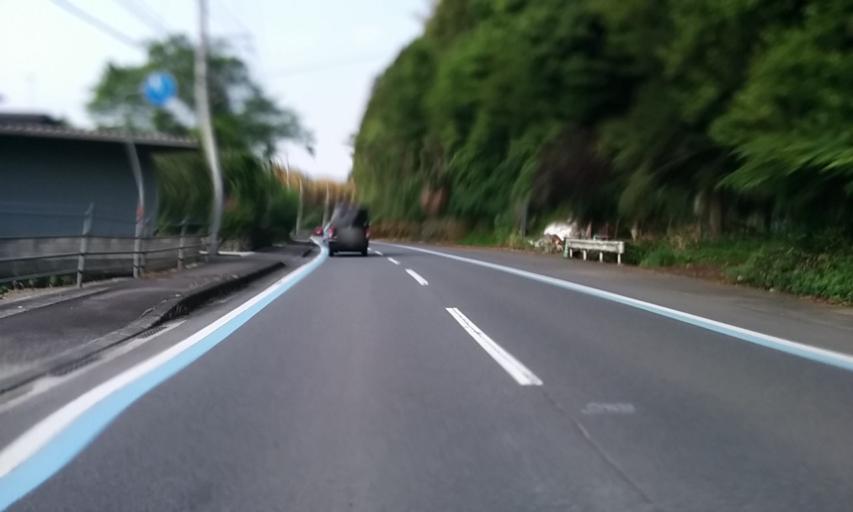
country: JP
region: Ehime
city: Saijo
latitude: 33.8802
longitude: 133.1772
